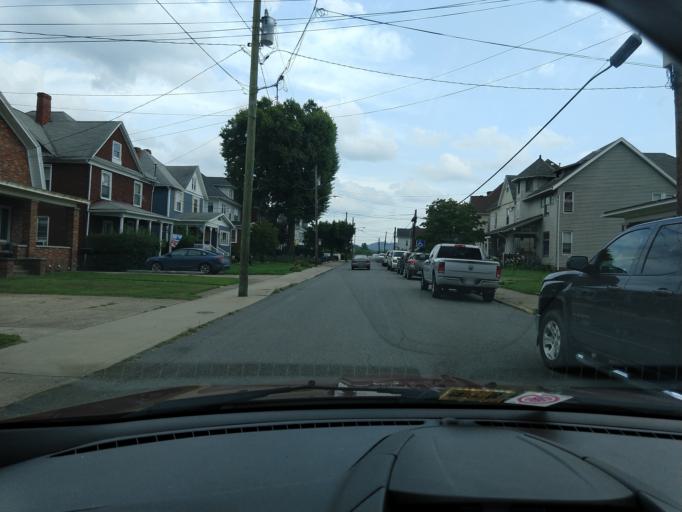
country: US
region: West Virginia
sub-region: Harrison County
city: Clarksburg
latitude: 39.2833
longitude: -80.3427
